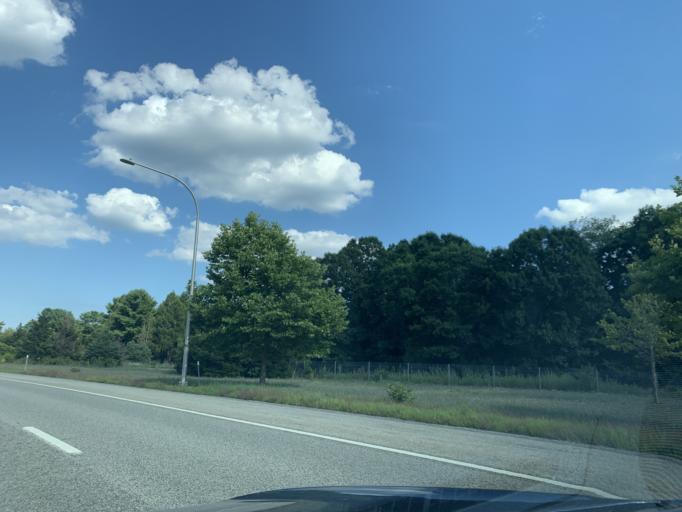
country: US
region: Rhode Island
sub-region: Washington County
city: North Kingstown
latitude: 41.6032
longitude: -71.4519
